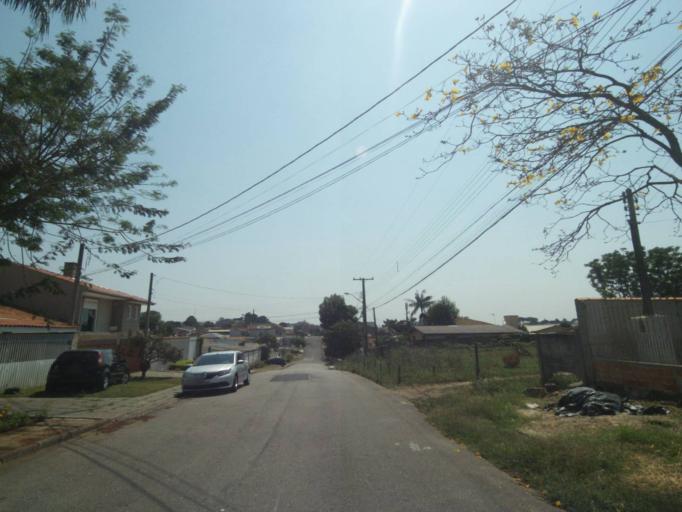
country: BR
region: Parana
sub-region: Sao Jose Dos Pinhais
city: Sao Jose dos Pinhais
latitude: -25.5070
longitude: -49.2720
